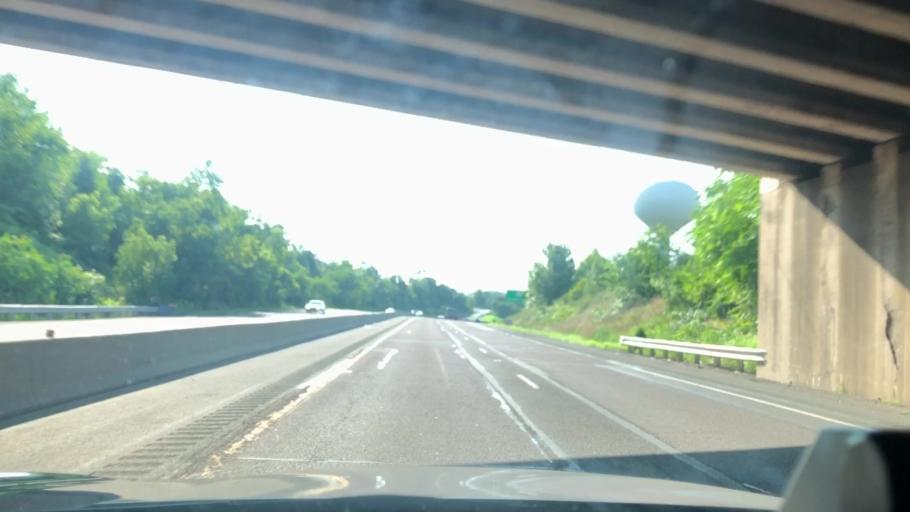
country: US
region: Pennsylvania
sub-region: Montgomery County
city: Souderton
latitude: 40.3149
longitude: -75.3038
